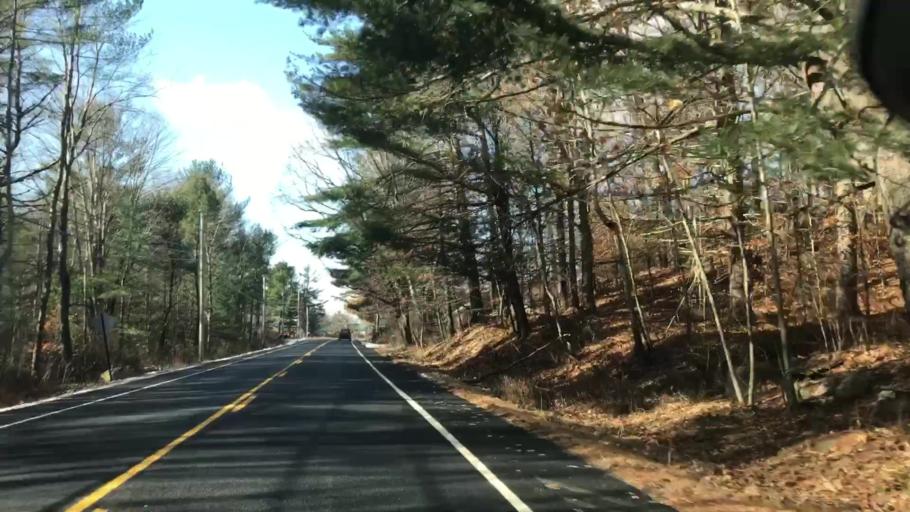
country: US
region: Maine
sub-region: Oxford County
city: Porter
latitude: 43.7952
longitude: -70.9262
